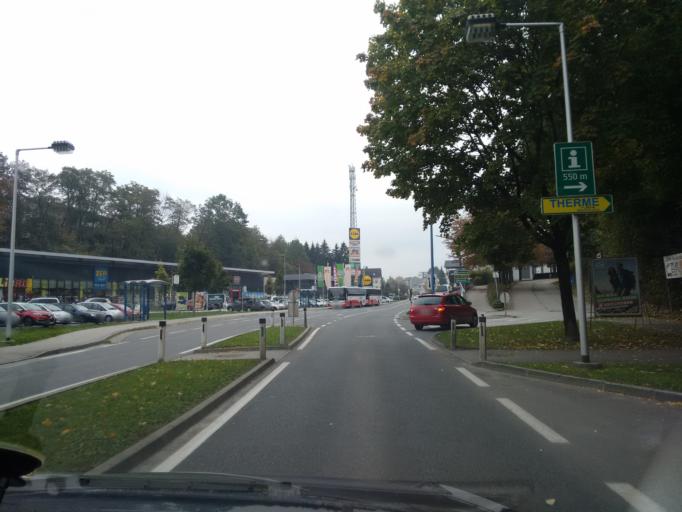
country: AT
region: Upper Austria
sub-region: Politischer Bezirk Steyr-Land
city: Bad Hall
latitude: 48.0372
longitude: 14.2094
